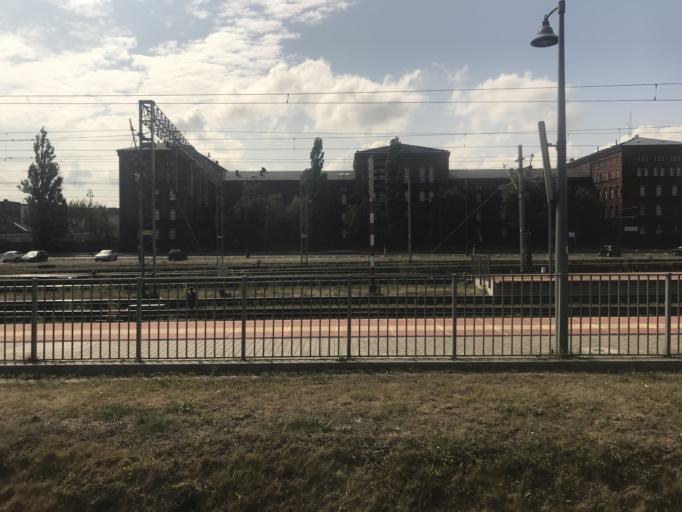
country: PL
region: Kujawsko-Pomorskie
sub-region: Bydgoszcz
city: Bydgoszcz
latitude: 53.1364
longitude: 17.9947
